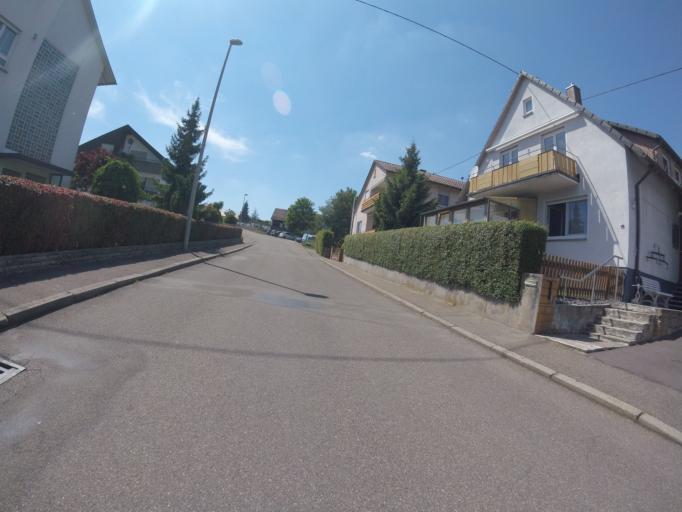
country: DE
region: Baden-Wuerttemberg
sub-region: Regierungsbezirk Stuttgart
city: Allmersbach im Tal
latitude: 48.9303
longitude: 9.4716
